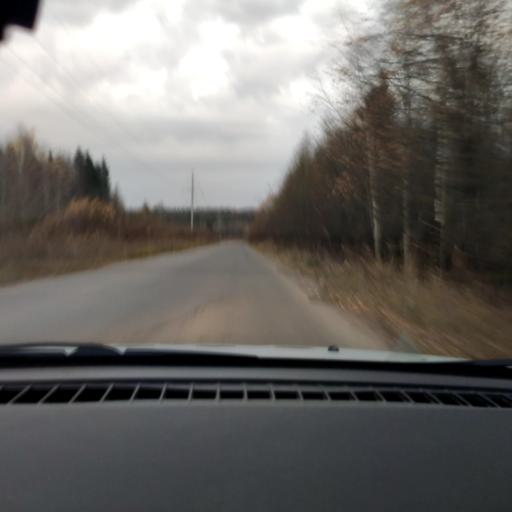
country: RU
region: Perm
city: Perm
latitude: 58.0898
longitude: 56.4153
